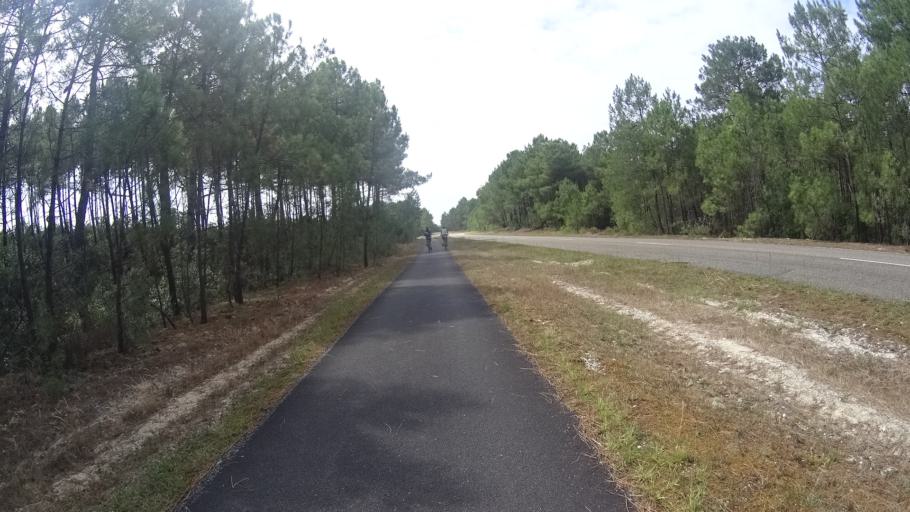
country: FR
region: Aquitaine
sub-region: Departement de la Gironde
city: Lacanau
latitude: 44.9845
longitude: -1.1517
